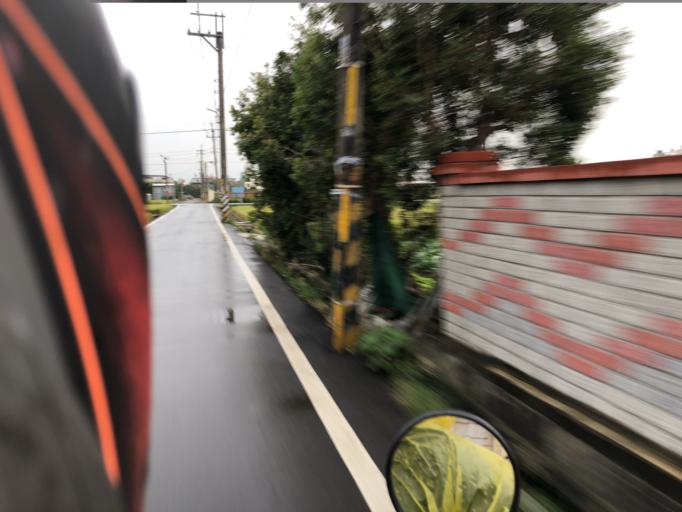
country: TW
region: Taiwan
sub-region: Hsinchu
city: Zhubei
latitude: 24.8512
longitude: 120.9901
